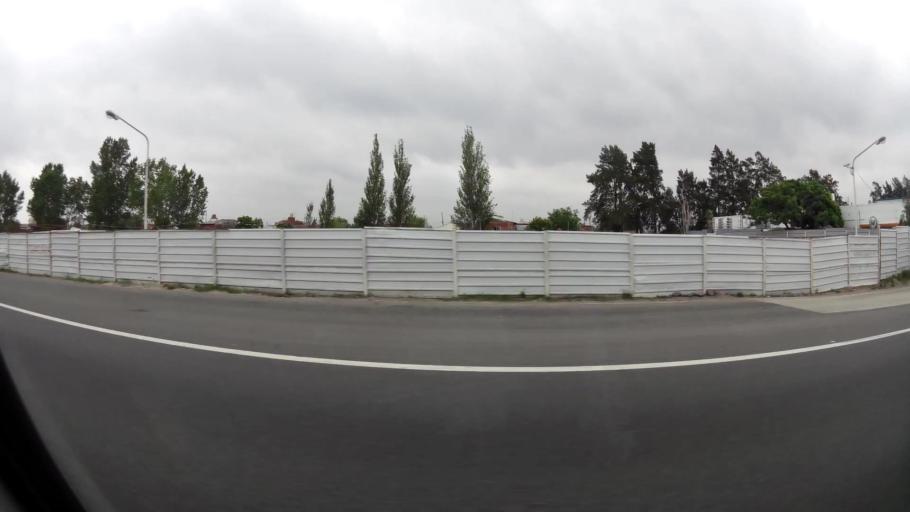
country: AR
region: Buenos Aires
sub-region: Partido de Quilmes
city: Quilmes
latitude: -34.6850
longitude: -58.3045
